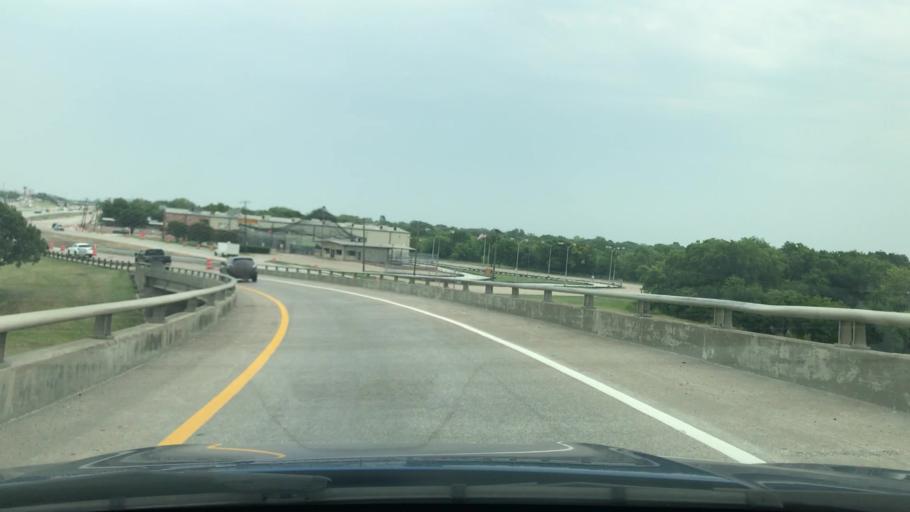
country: US
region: Texas
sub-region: Dallas County
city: Mesquite
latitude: 32.7918
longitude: -96.6240
